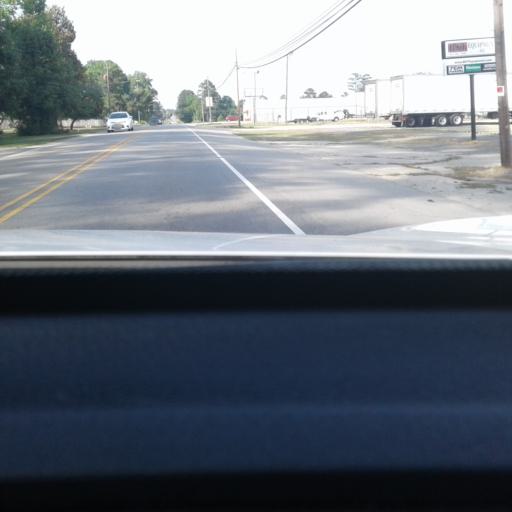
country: US
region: North Carolina
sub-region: Harnett County
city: Dunn
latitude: 35.3214
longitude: -78.6060
